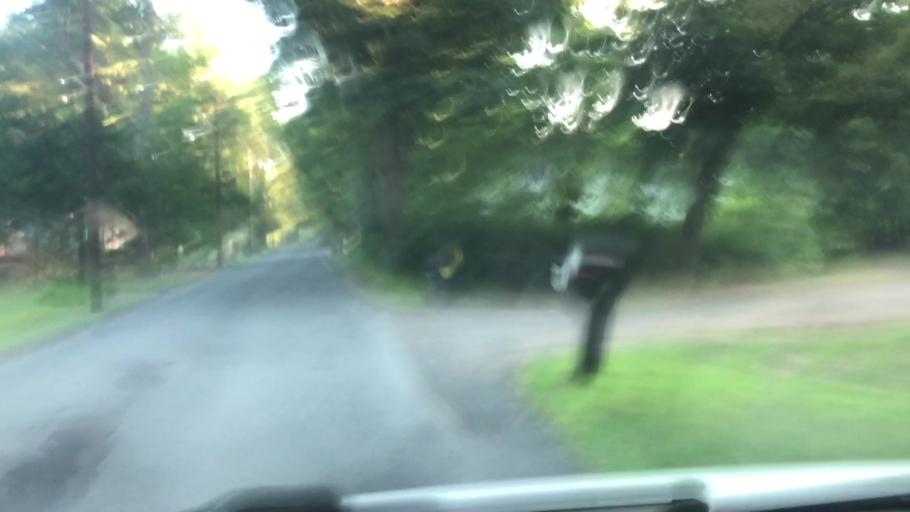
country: US
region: Massachusetts
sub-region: Hampshire County
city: Easthampton
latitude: 42.2935
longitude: -72.7166
